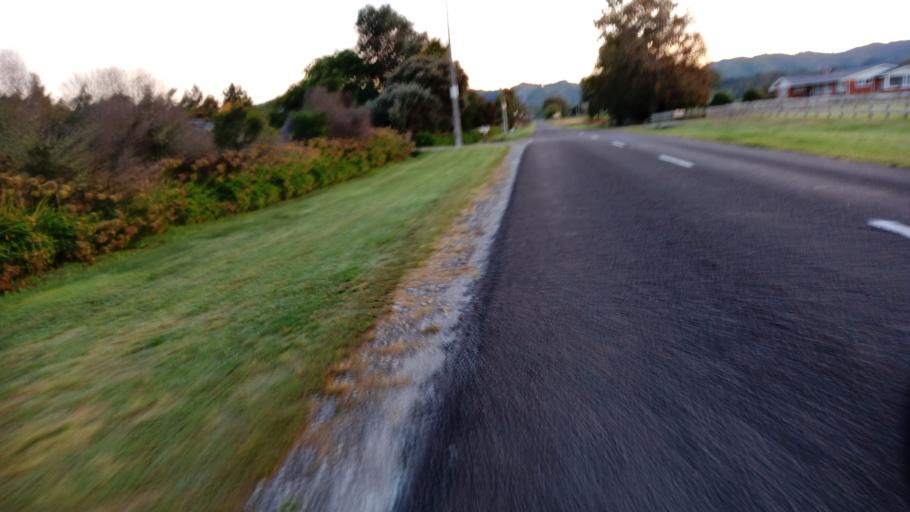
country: NZ
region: Gisborne
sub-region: Gisborne District
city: Gisborne
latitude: -38.6422
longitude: 177.9822
